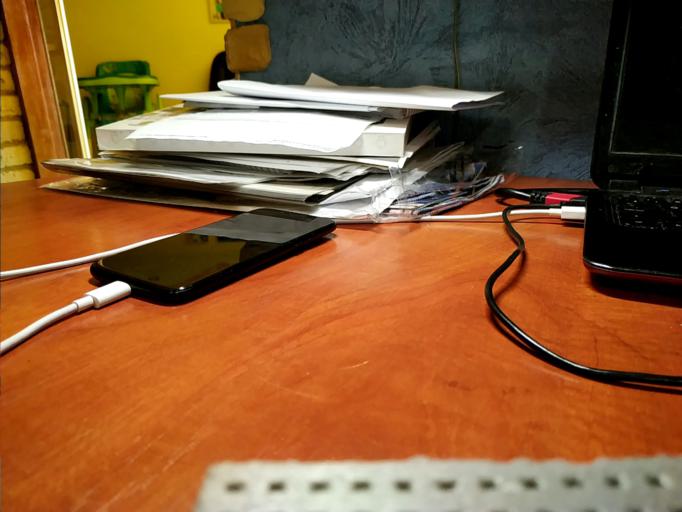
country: RU
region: Tverskaya
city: Kalashnikovo
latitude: 57.3982
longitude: 35.2446
